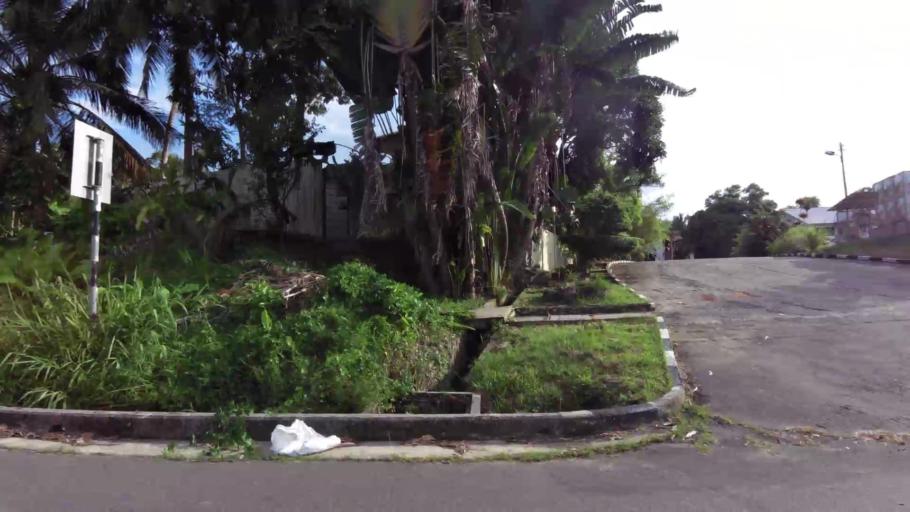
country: BN
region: Brunei and Muara
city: Bandar Seri Begawan
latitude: 4.9655
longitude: 114.9824
